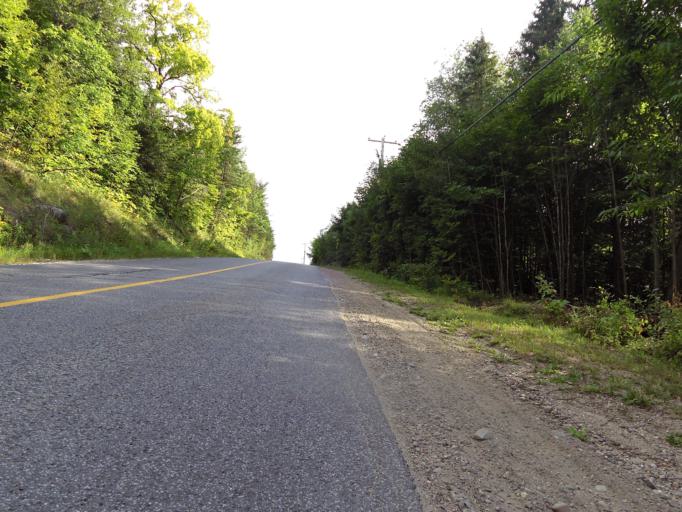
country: CA
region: Quebec
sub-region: Outaouais
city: Wakefield
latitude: 45.6519
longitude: -76.0161
